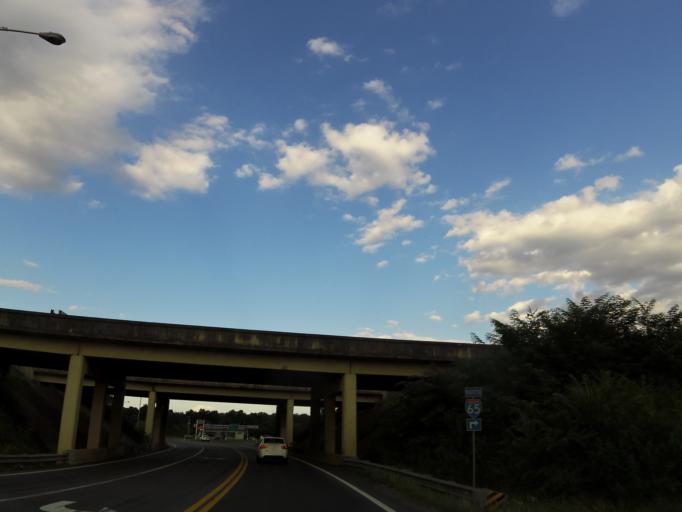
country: US
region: Tennessee
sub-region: Maury County
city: Spring Hill
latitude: 35.6427
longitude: -86.8943
